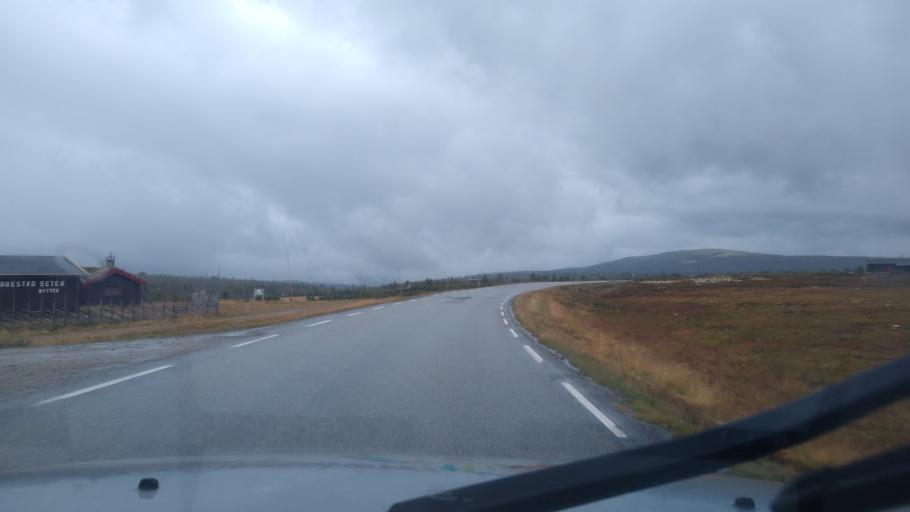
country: NO
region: Oppland
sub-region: Ringebu
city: Ringebu
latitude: 61.6669
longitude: 10.1237
